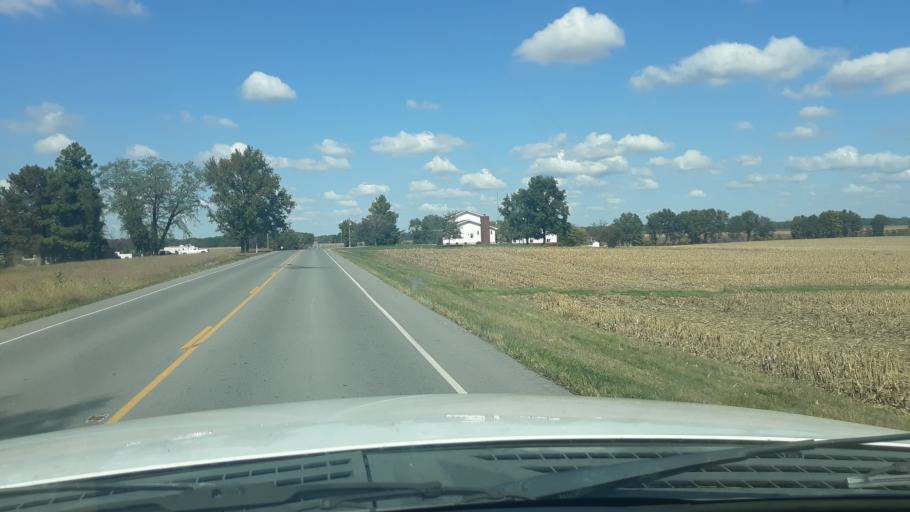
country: US
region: Illinois
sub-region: Saline County
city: Eldorado
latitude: 37.7936
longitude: -88.4848
